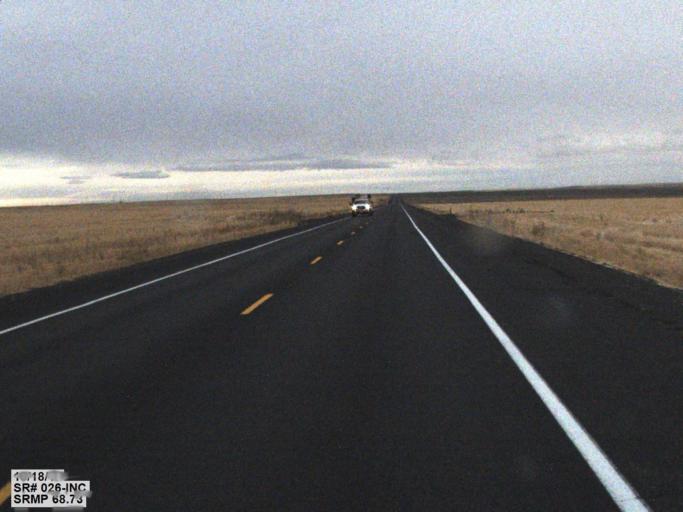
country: US
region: Washington
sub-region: Franklin County
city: Connell
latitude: 46.7946
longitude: -118.5866
